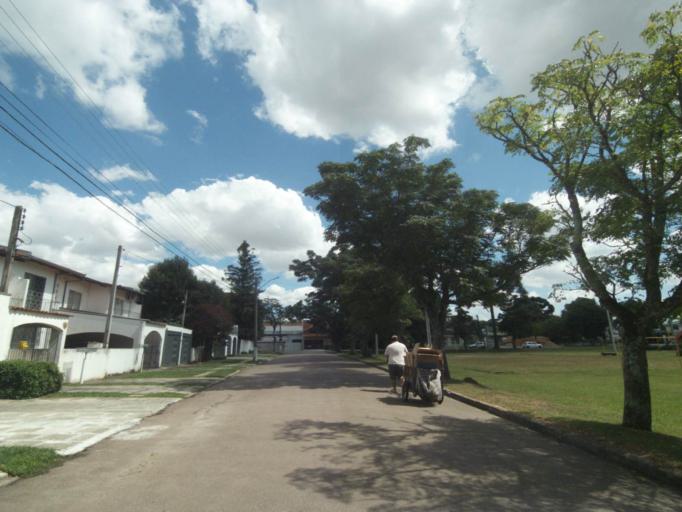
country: BR
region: Parana
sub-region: Pinhais
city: Pinhais
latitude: -25.4322
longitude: -49.2154
